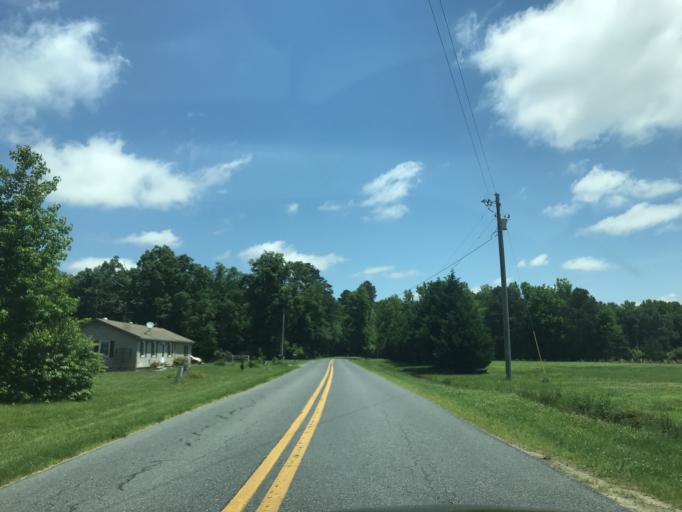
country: US
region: Maryland
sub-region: Caroline County
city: Federalsburg
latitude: 38.7408
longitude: -75.7148
